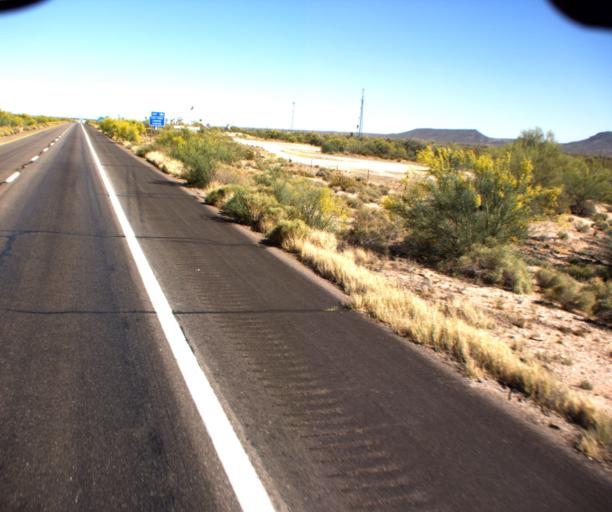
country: US
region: Arizona
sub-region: Pinal County
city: Maricopa
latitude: 32.8347
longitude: -112.1436
